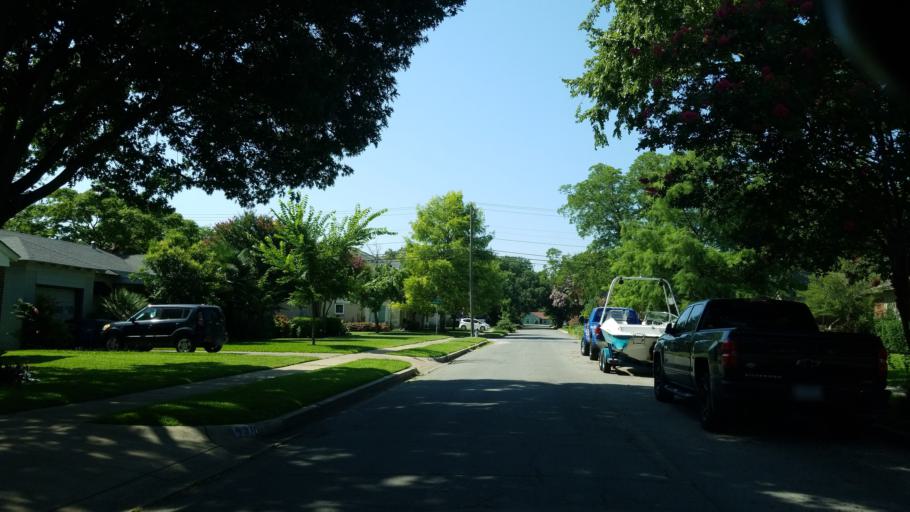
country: US
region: Texas
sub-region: Dallas County
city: Highland Park
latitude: 32.8389
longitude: -96.7655
